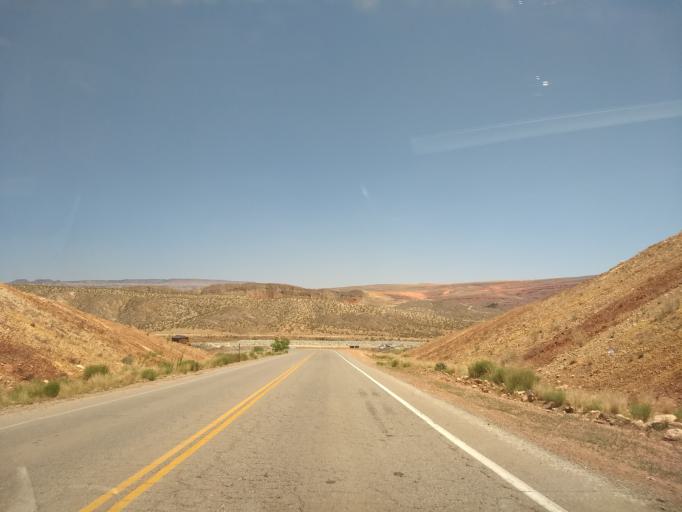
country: US
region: Utah
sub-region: Washington County
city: Washington
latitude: 37.1356
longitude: -113.4565
